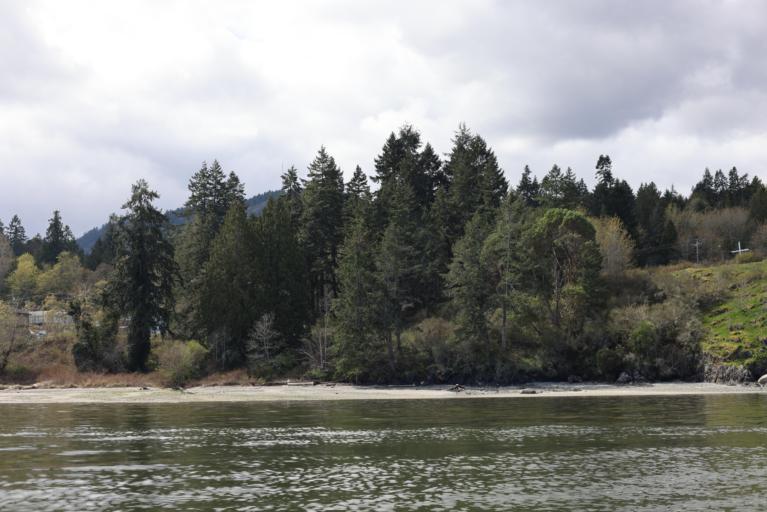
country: CA
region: British Columbia
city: North Saanich
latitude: 48.6173
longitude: -123.5186
